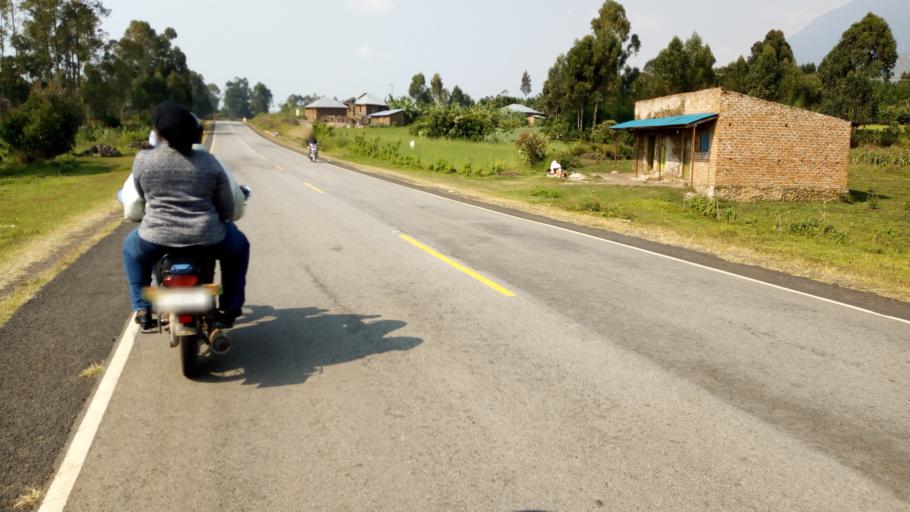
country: UG
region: Western Region
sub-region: Kisoro District
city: Kisoro
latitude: -1.3217
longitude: 29.7285
